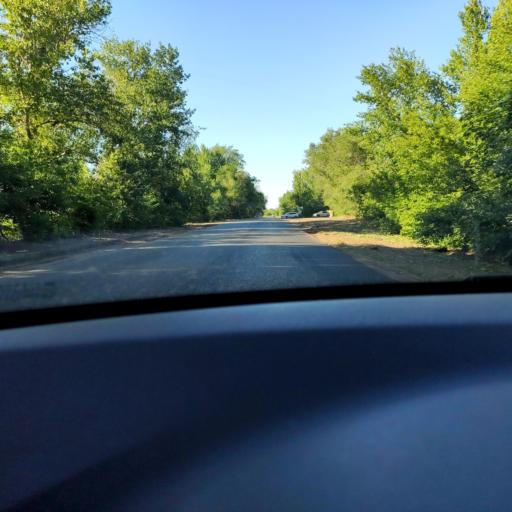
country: RU
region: Samara
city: Samara
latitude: 53.1243
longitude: 50.2346
